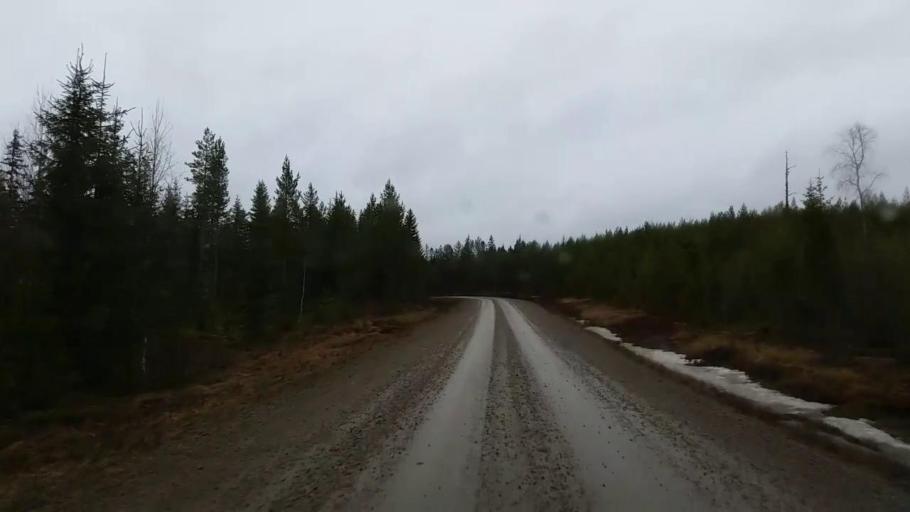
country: SE
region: Gaevleborg
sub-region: Ljusdals Kommun
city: Farila
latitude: 62.1152
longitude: 15.6903
